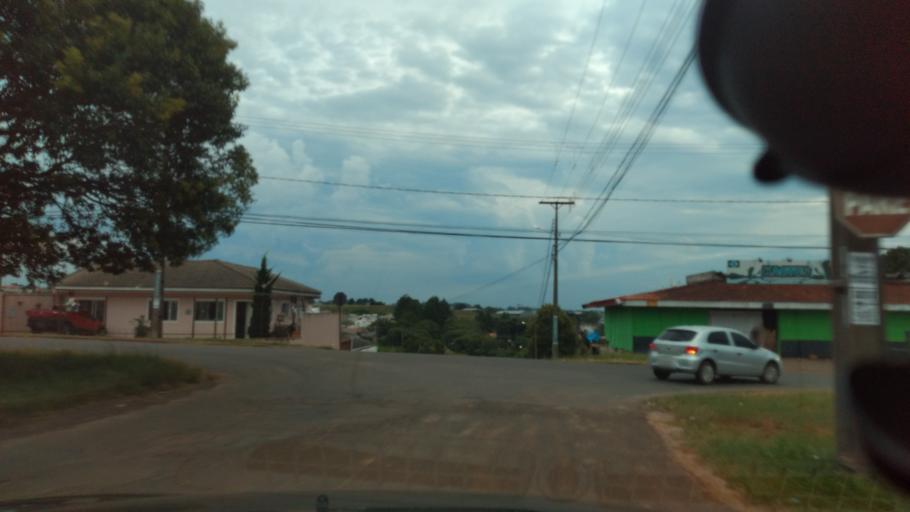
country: BR
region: Parana
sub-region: Guarapuava
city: Guarapuava
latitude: -25.3923
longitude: -51.4856
